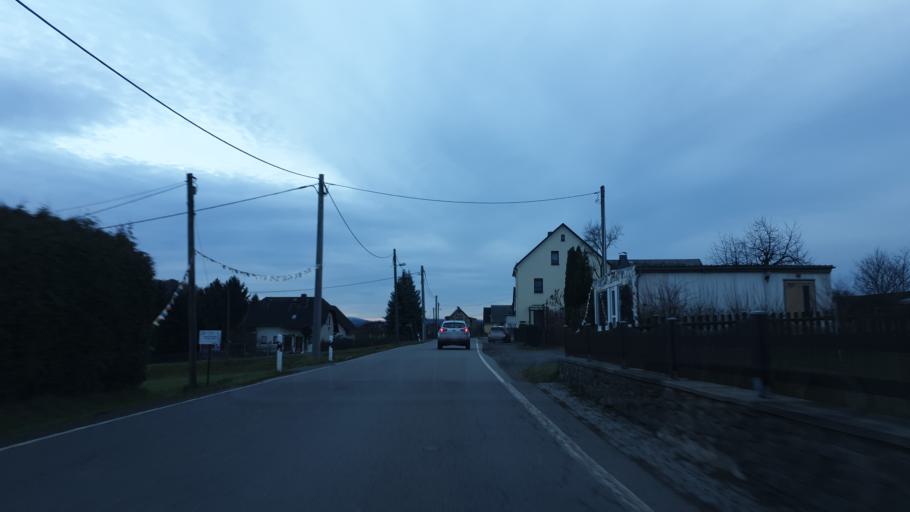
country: DE
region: Saxony
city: Hartenstein
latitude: 50.6842
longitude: 12.6695
